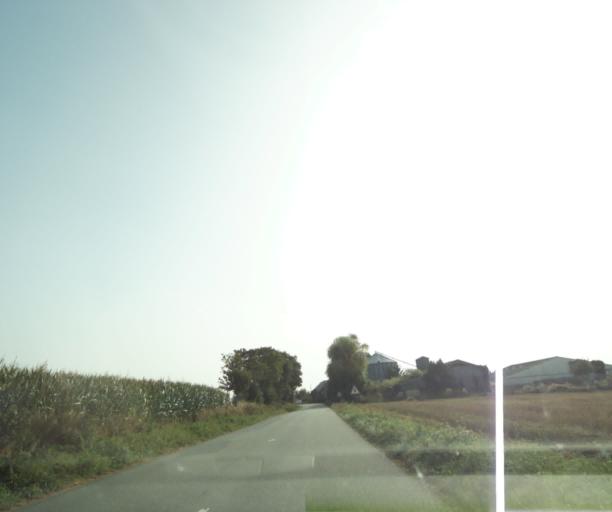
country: FR
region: Brittany
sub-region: Departement des Cotes-d'Armor
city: Jugon-les-Lacs
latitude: 48.4193
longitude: -2.3136
